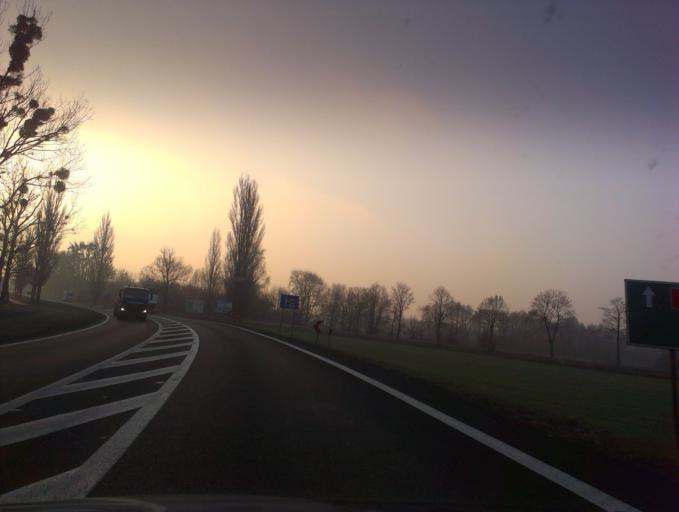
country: PL
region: Greater Poland Voivodeship
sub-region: Powiat obornicki
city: Rogozno
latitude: 52.7668
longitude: 16.9583
